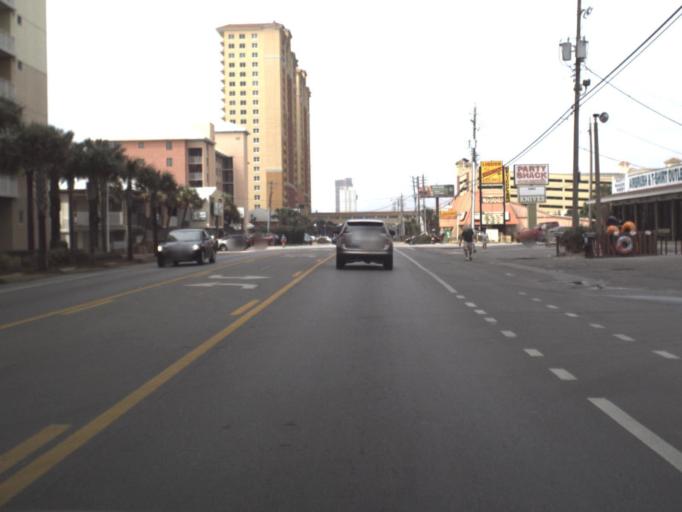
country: US
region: Florida
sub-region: Bay County
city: Laguna Beach
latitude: 30.2125
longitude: -85.8706
